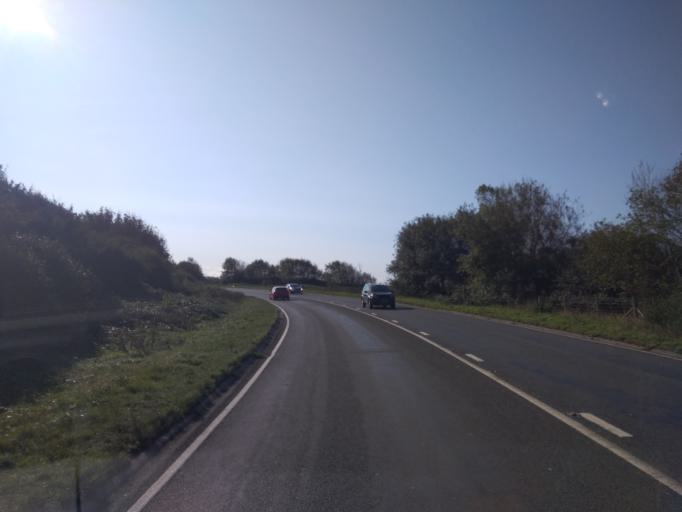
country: GB
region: England
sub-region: East Sussex
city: Newhaven
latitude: 50.7955
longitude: 0.0667
